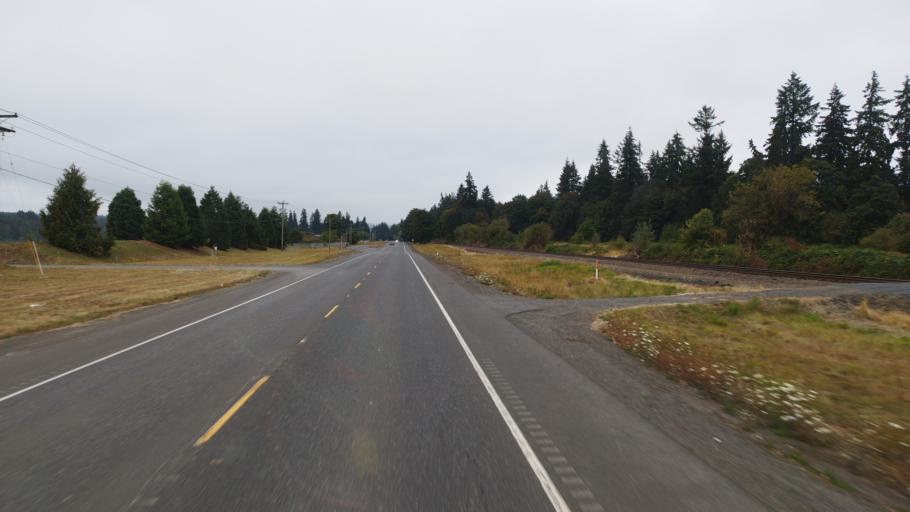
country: US
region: Oregon
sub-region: Columbia County
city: Columbia City
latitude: 45.9185
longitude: -122.8306
